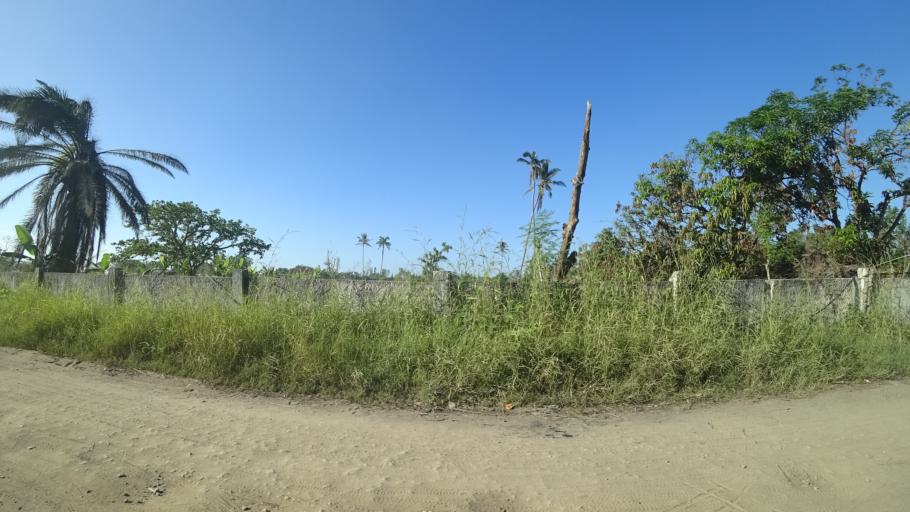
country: MZ
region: Sofala
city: Beira
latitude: -19.7646
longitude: 34.8974
